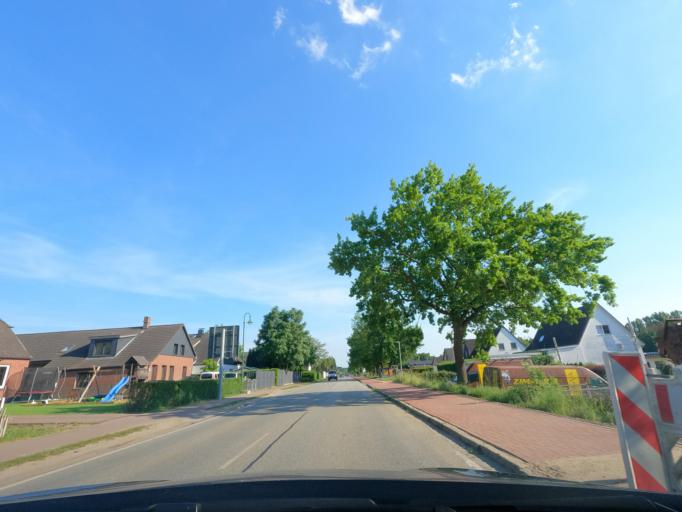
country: DE
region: Schleswig-Holstein
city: Gross Nordende
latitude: 53.7079
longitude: 9.6478
